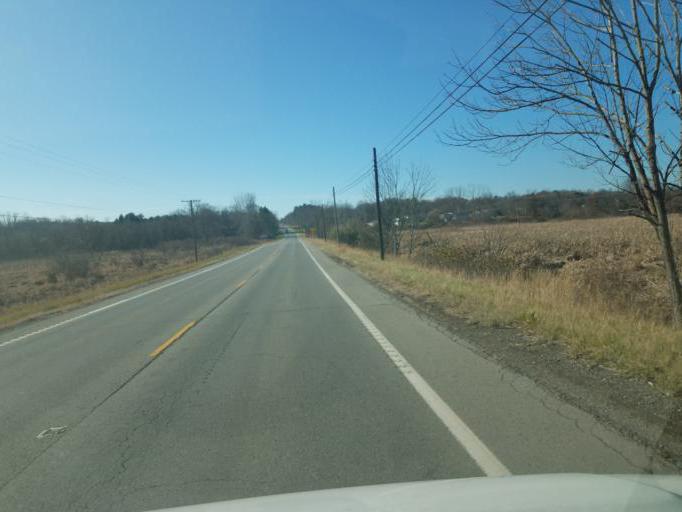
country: US
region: Ohio
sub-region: Richland County
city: Lincoln Heights
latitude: 40.8062
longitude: -82.4250
